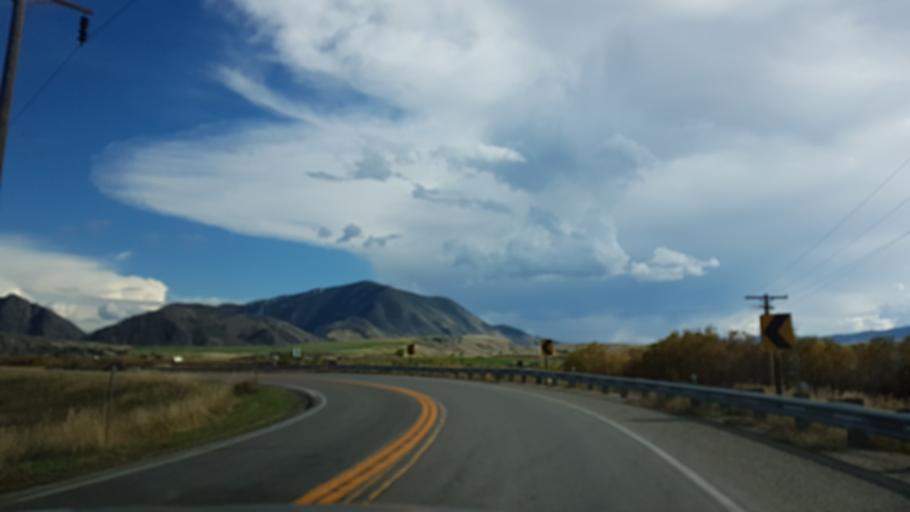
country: US
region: Montana
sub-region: Jefferson County
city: Whitehall
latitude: 45.8531
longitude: -111.9500
